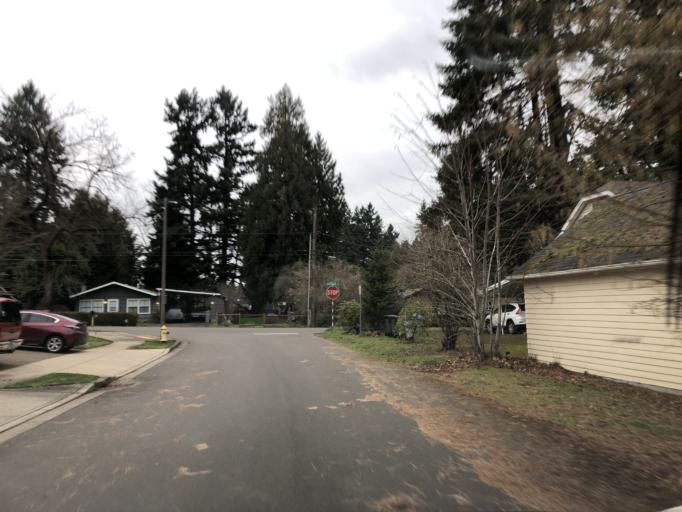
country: US
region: Oregon
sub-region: Washington County
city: Tigard
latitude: 45.4287
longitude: -122.7882
